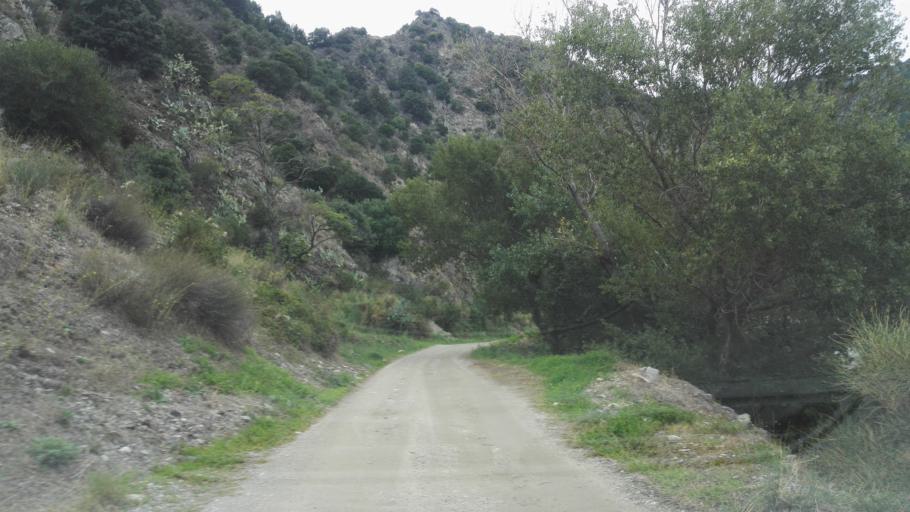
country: IT
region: Calabria
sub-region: Provincia di Reggio Calabria
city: Caulonia
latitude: 38.4213
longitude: 16.3757
